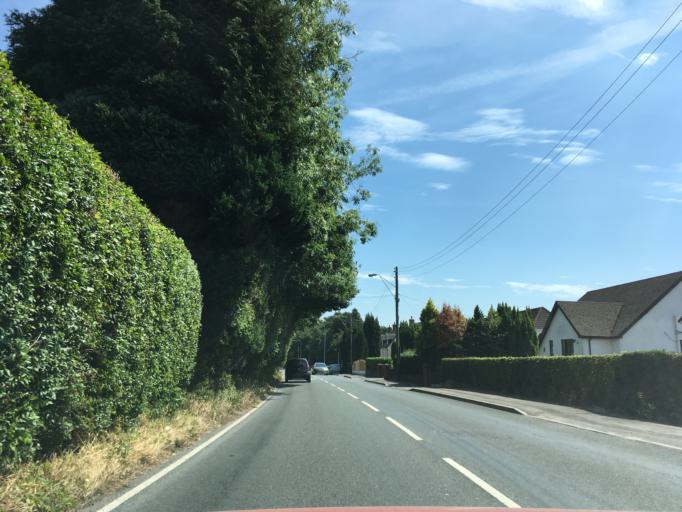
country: GB
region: Wales
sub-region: Caerphilly County Borough
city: Risca
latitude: 51.5997
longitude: -3.0710
